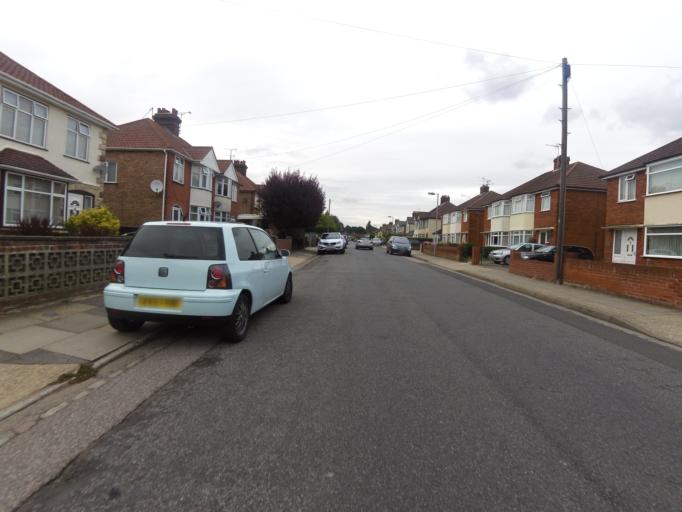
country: GB
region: England
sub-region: Suffolk
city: Ipswich
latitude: 52.0642
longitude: 1.1739
